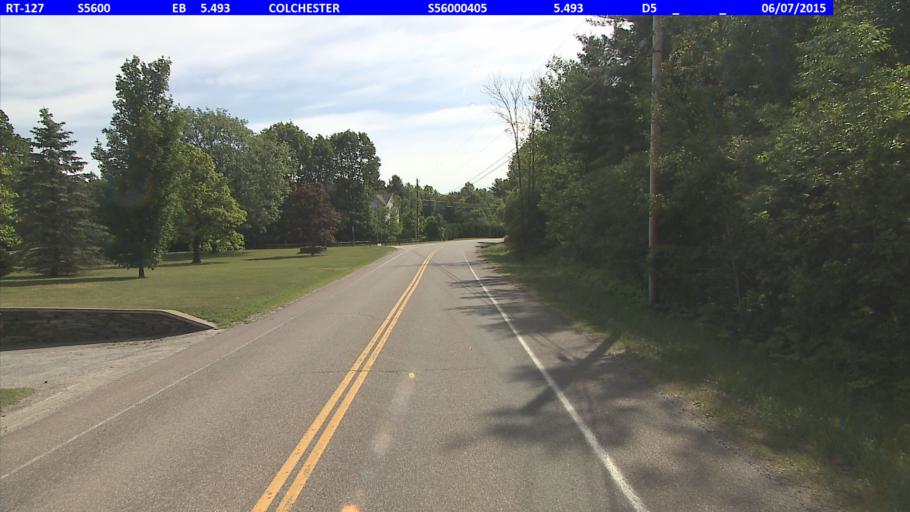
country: US
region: Vermont
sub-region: Chittenden County
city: Colchester
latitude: 44.5310
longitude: -73.1796
